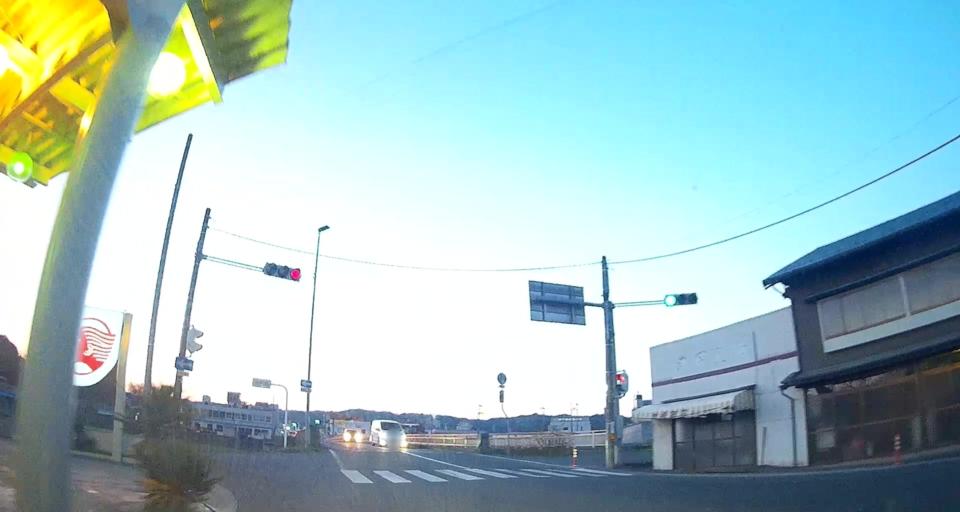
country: JP
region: Aomori
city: Hachinohe
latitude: 40.1866
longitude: 141.7717
